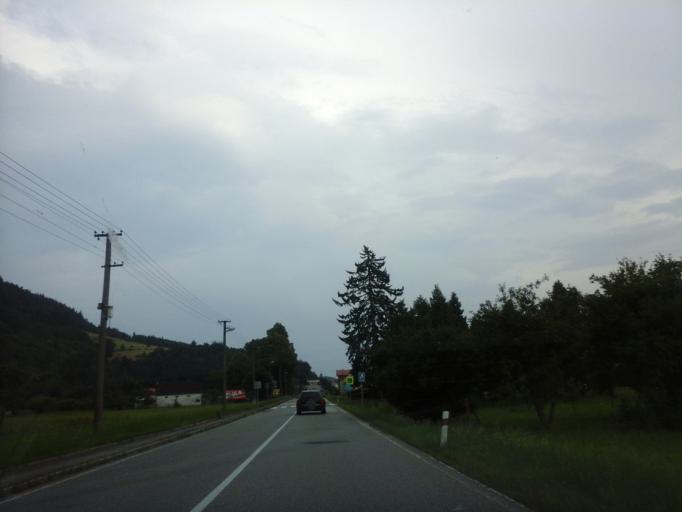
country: CZ
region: Pardubicky
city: Brnenec
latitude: 49.6001
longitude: 16.5343
